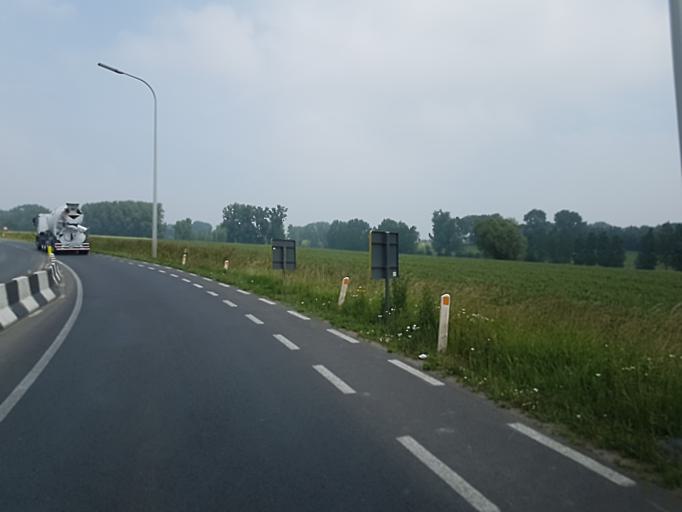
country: BE
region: Flanders
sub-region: Provincie Oost-Vlaanderen
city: Sint-Maria-Lierde
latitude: 50.8416
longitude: 3.8706
